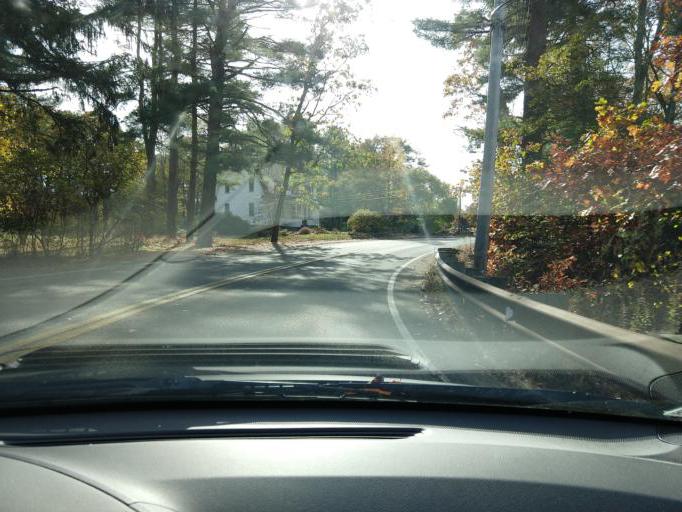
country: US
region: Massachusetts
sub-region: Middlesex County
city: West Concord
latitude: 42.4714
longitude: -71.3871
